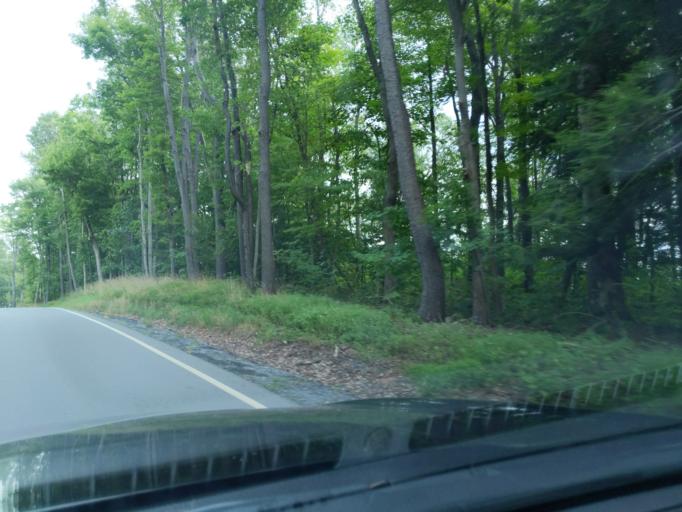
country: US
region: Pennsylvania
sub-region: Cambria County
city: Beaverdale
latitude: 40.3098
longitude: -78.5743
